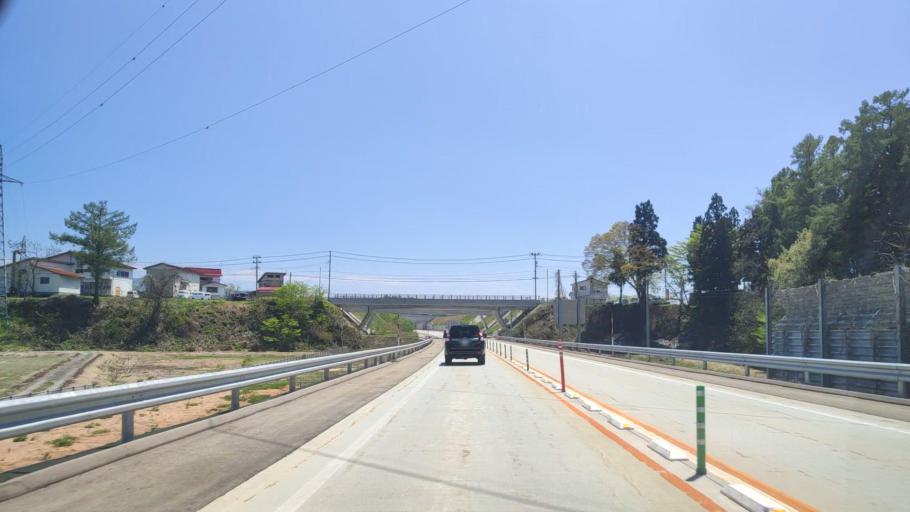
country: JP
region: Yamagata
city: Obanazawa
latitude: 38.5993
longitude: 140.3864
